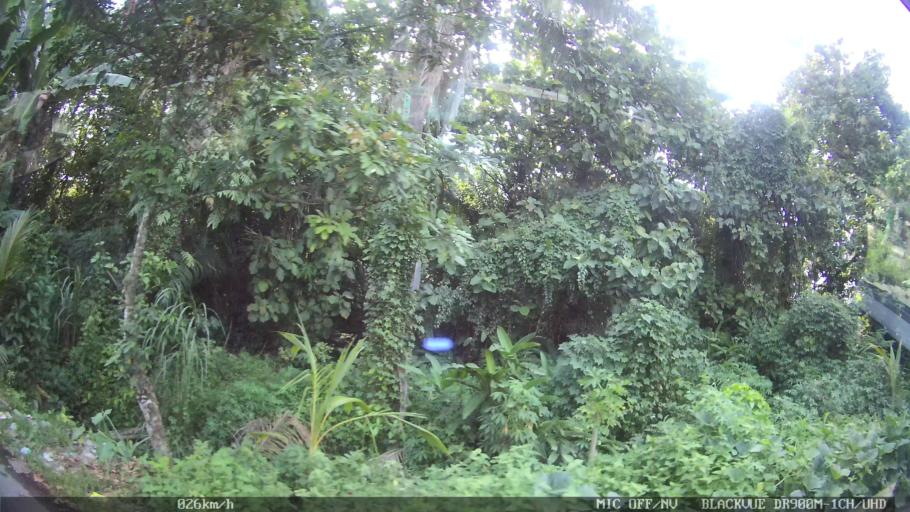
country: ID
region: North Sumatra
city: Binjai
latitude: 3.6494
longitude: 98.5178
